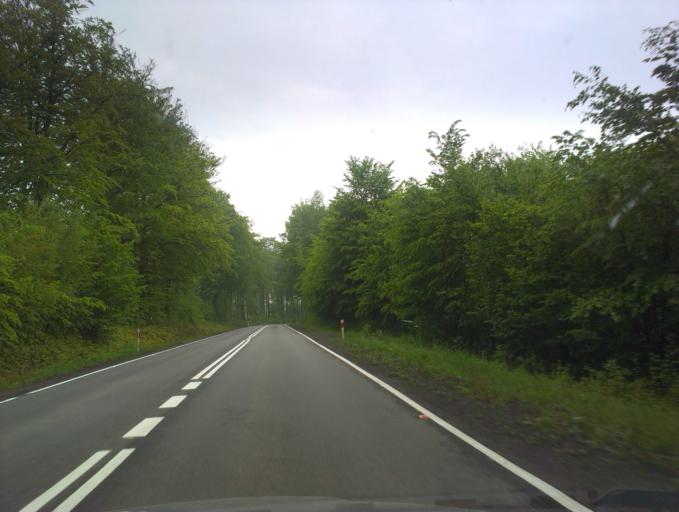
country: PL
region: West Pomeranian Voivodeship
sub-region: Powiat koszalinski
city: Bobolice
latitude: 53.9217
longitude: 16.6025
